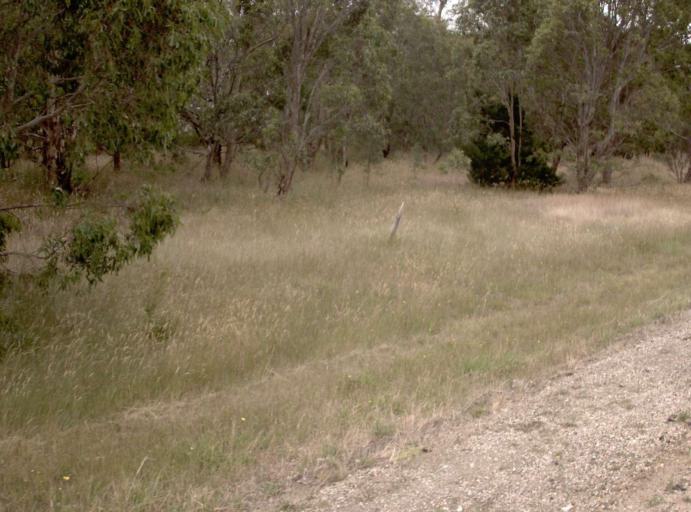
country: AU
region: Victoria
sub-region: Wellington
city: Sale
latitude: -38.1662
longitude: 147.0626
